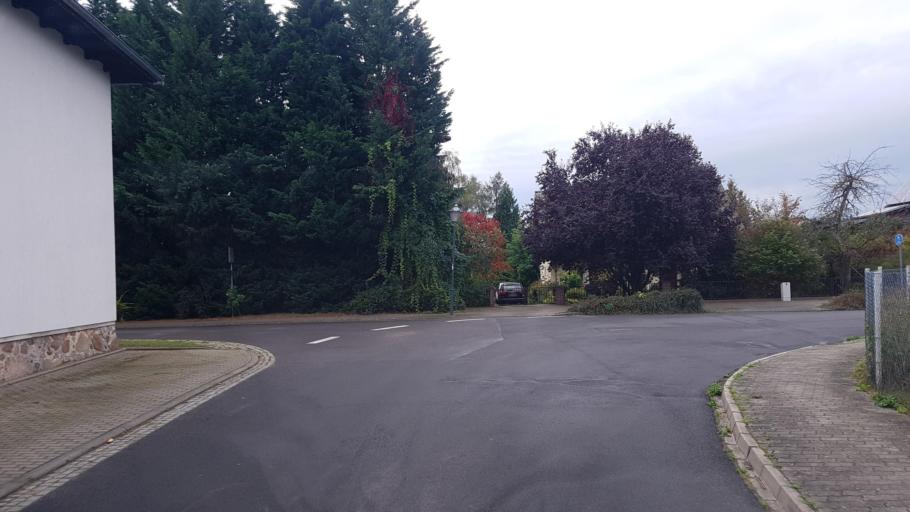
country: DE
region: Brandenburg
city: Golssen
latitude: 51.9687
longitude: 13.6074
